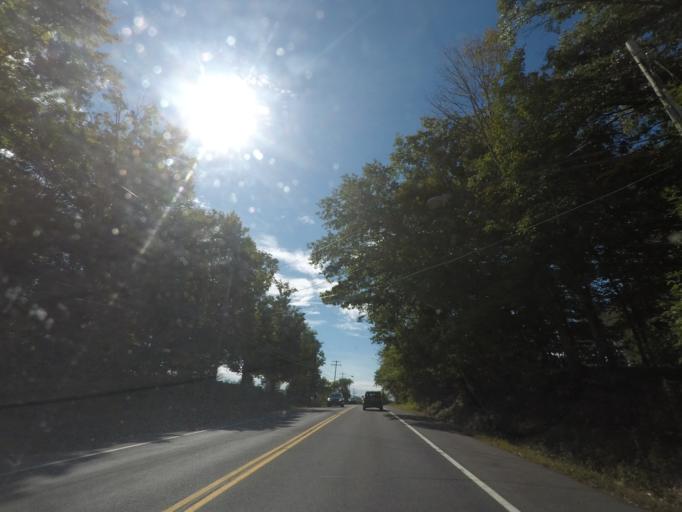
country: US
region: New York
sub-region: Rensselaer County
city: East Greenbush
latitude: 42.6030
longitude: -73.7076
